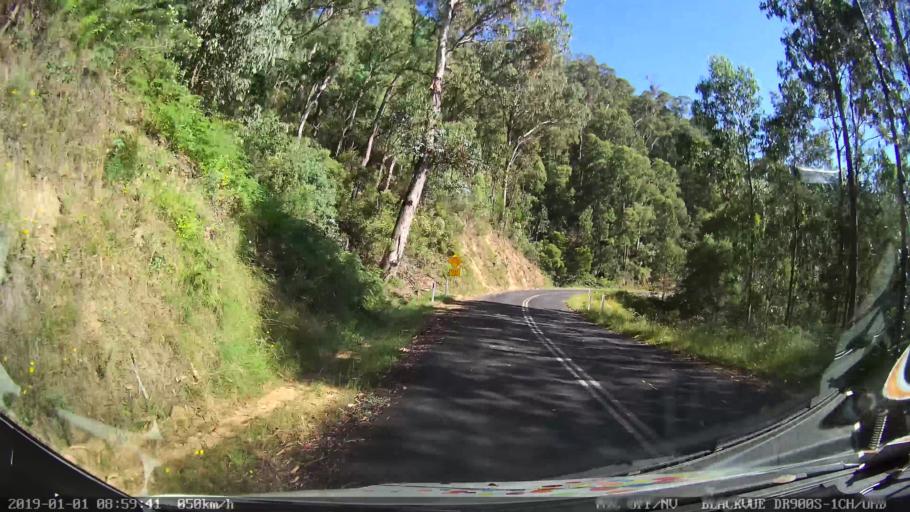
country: AU
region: New South Wales
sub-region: Snowy River
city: Jindabyne
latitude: -36.2395
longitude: 148.1791
